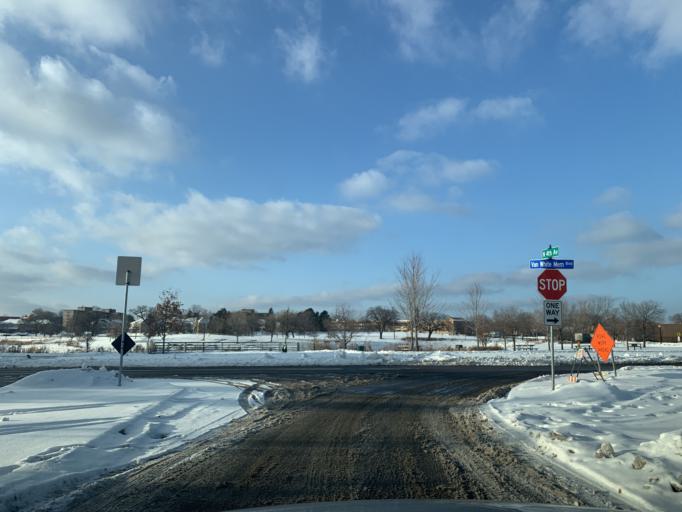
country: US
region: Minnesota
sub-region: Hennepin County
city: Minneapolis
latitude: 44.9818
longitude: -93.2930
